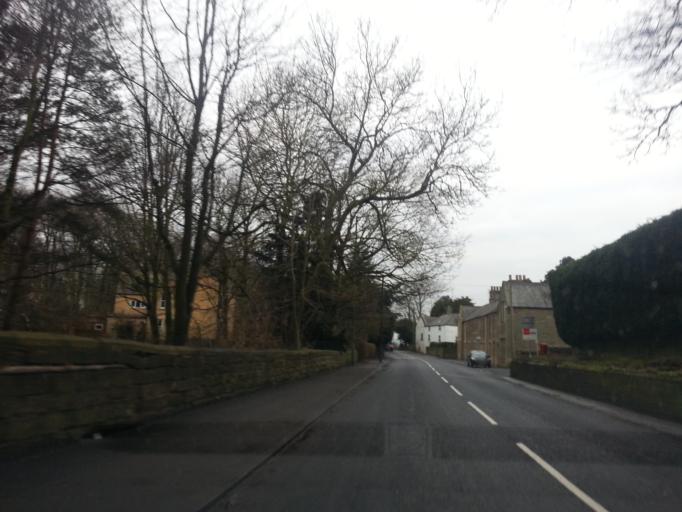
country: GB
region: England
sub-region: County Durham
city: Chester-le-Street
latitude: 54.8728
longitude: -1.5632
